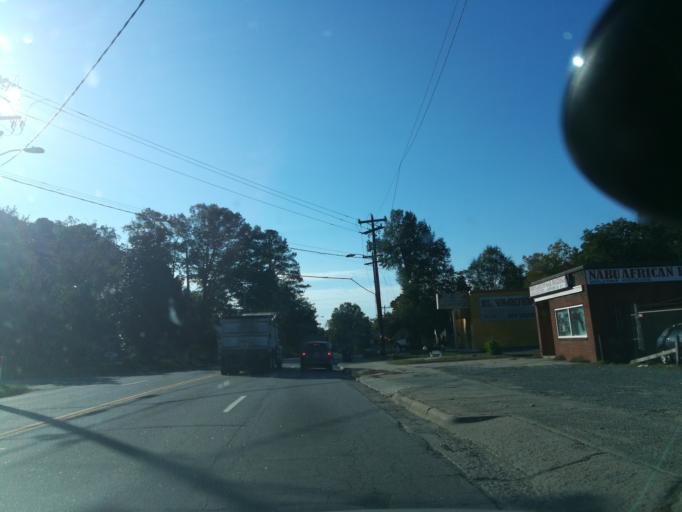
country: US
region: North Carolina
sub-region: Durham County
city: Durham
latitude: 36.0273
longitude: -78.8899
